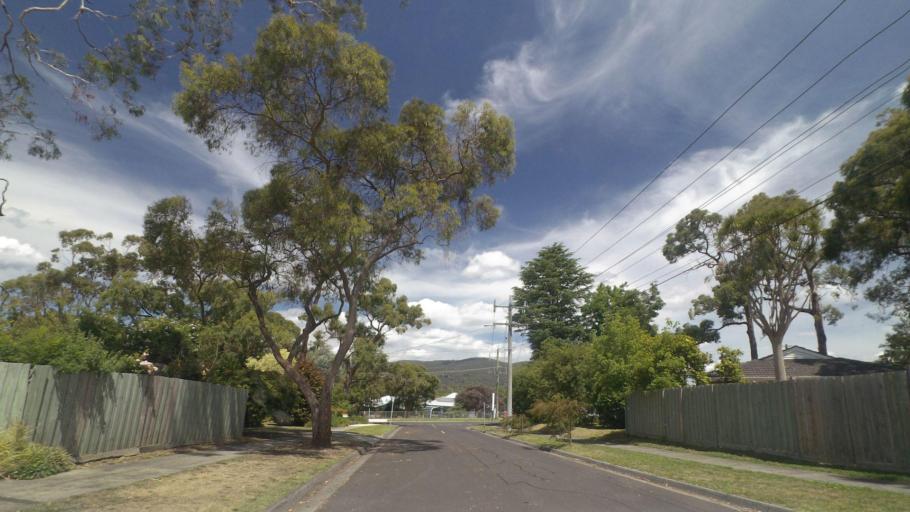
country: AU
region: Victoria
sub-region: Maroondah
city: Bayswater North
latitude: -37.8444
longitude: 145.2953
